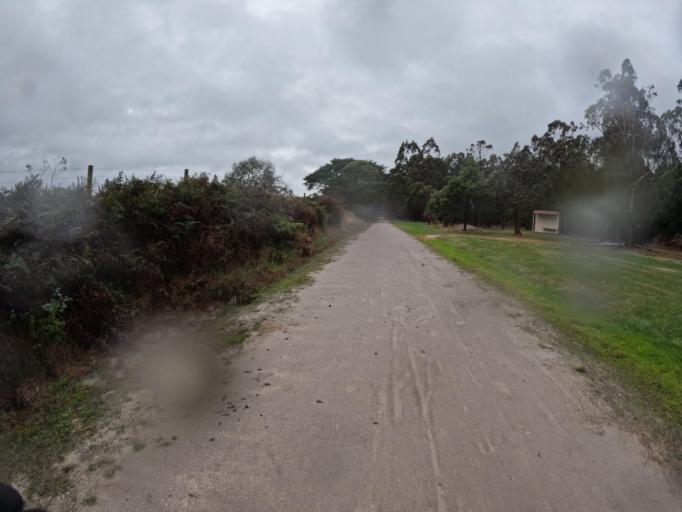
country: AU
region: Victoria
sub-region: Latrobe
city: Morwell
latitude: -38.6896
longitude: 146.1385
